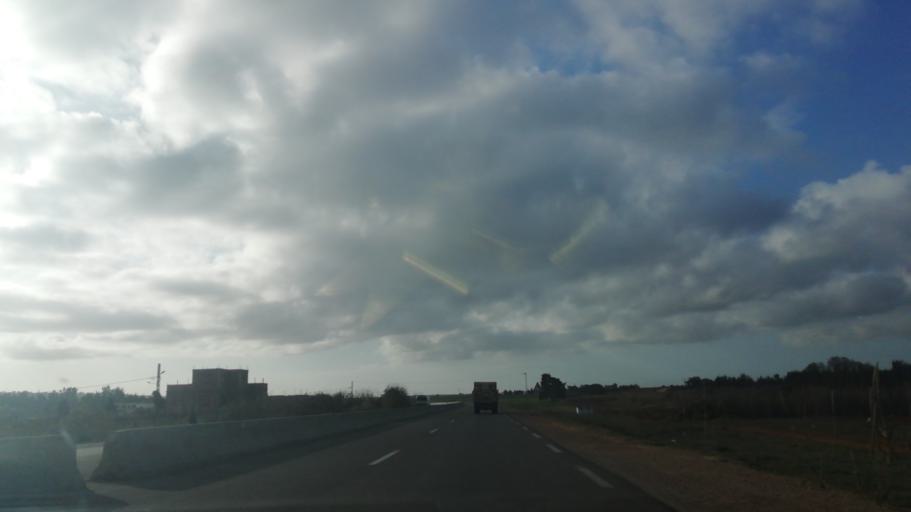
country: DZ
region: Mostaganem
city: Mostaganem
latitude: 36.1021
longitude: 0.2659
